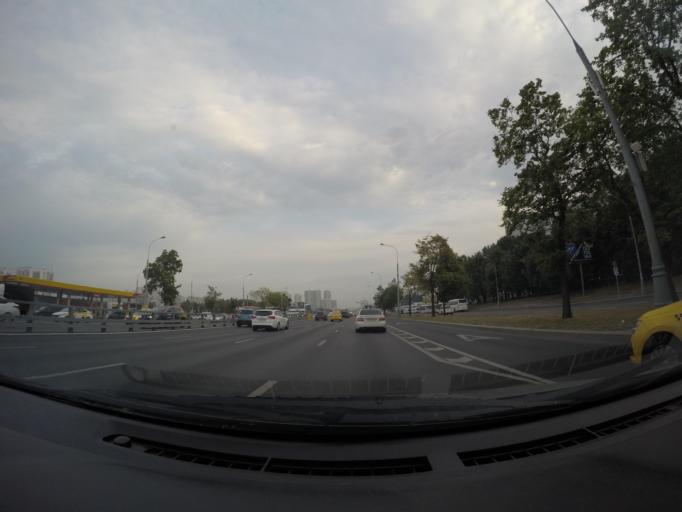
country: RU
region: Moscow
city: Orekhovo-Borisovo
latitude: 55.6128
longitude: 37.7164
